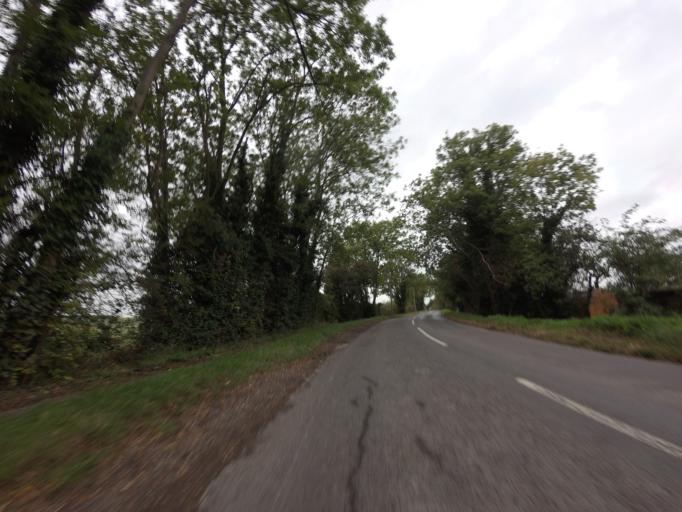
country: GB
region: England
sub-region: Cambridgeshire
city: Comberton
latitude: 52.1523
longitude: 0.0155
